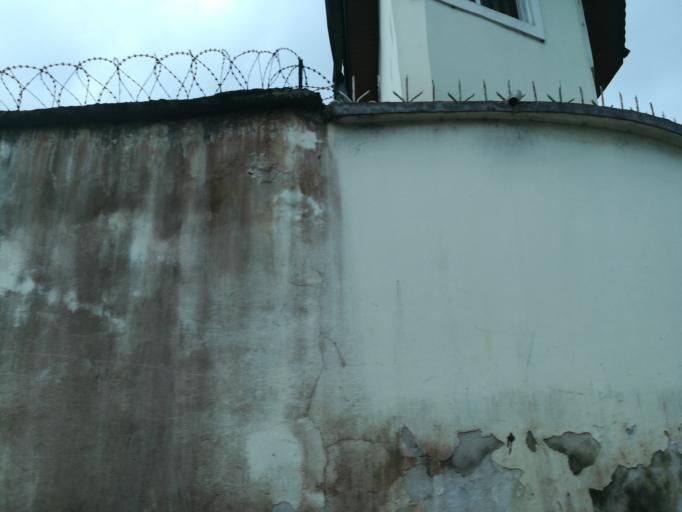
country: NG
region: Rivers
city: Port Harcourt
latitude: 4.8220
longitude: 7.0640
